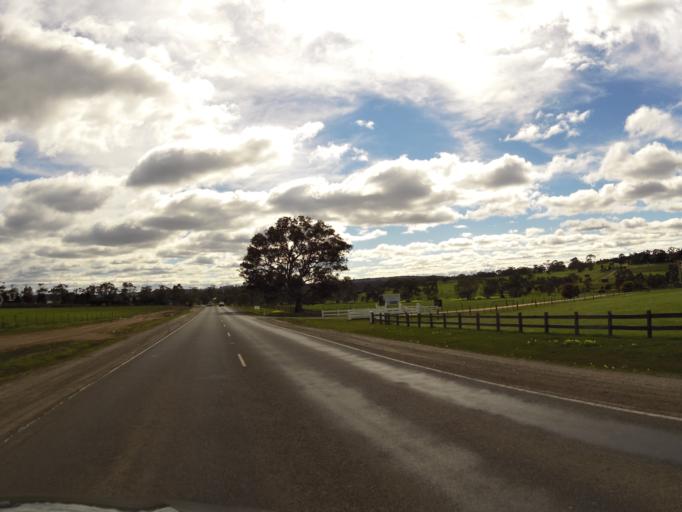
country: AU
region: Victoria
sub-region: Hume
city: Greenvale
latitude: -37.6426
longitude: 144.8342
